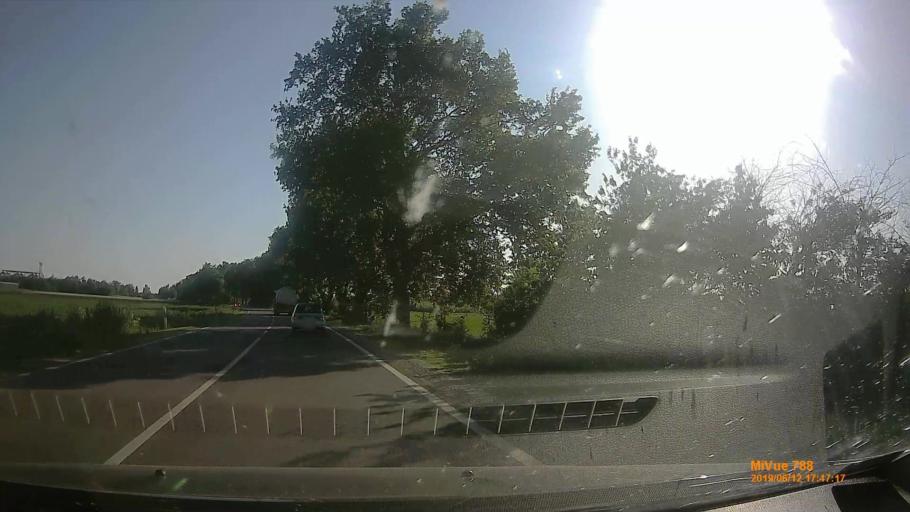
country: HU
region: Csongrad
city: Roszke
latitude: 46.2308
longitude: 20.0802
